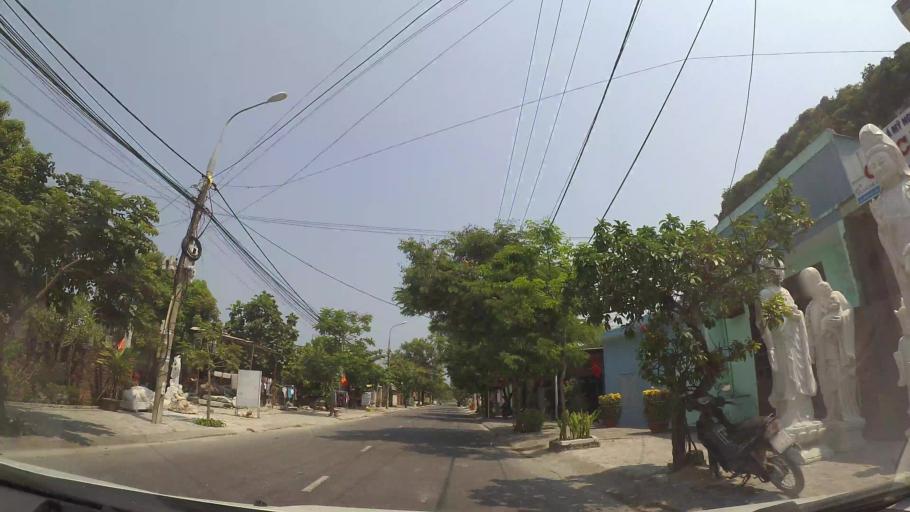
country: VN
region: Da Nang
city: Ngu Hanh Son
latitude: 16.0009
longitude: 108.2616
